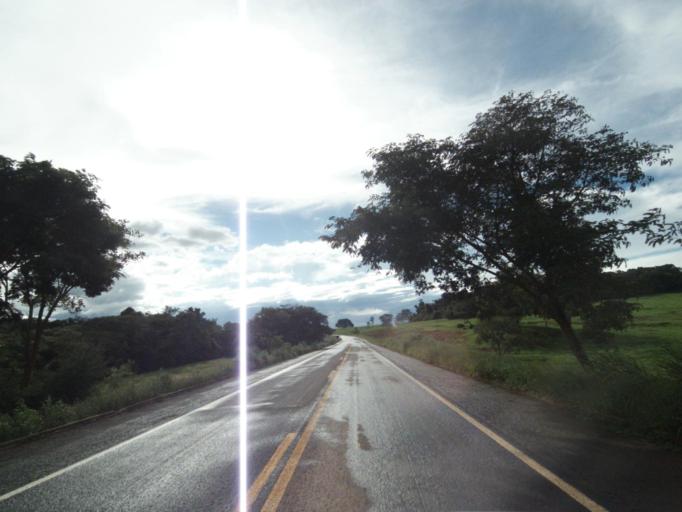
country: BR
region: Goias
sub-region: Itaberai
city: Itaberai
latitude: -15.9079
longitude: -49.5666
